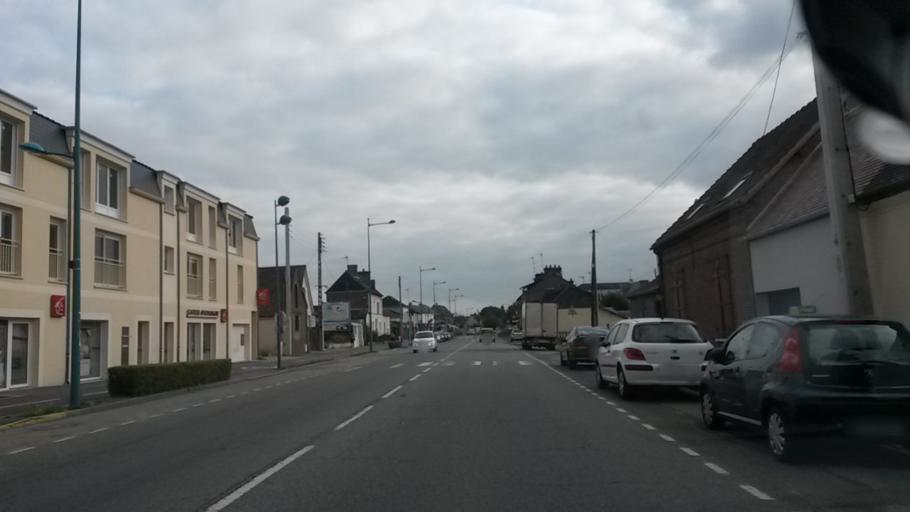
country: FR
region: Haute-Normandie
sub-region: Departement de l'Eure
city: Gravigny
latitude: 49.0490
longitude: 1.1637
